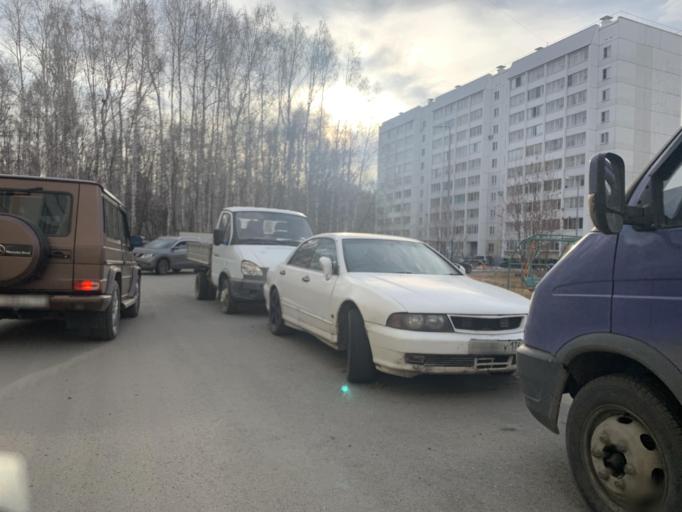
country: RU
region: Chelyabinsk
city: Roshchino
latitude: 55.2071
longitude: 61.3066
